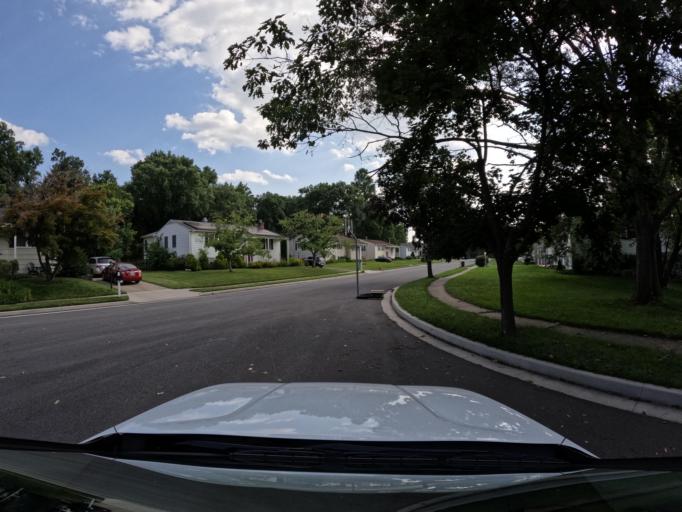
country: US
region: Maryland
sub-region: Baltimore County
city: Lutherville
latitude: 39.4165
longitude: -76.6417
